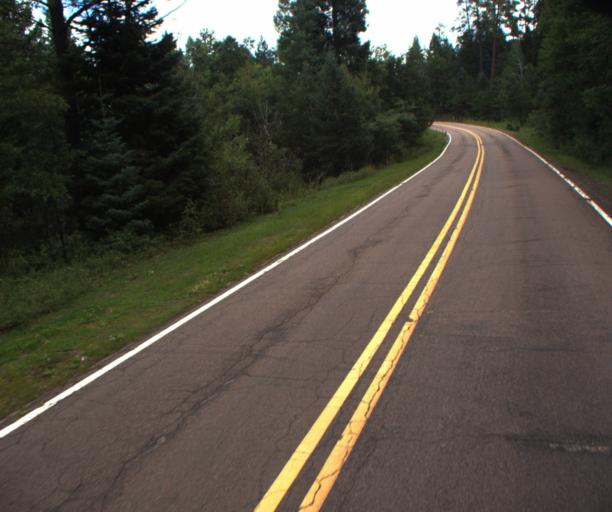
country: US
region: Arizona
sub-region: Navajo County
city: Pinetop-Lakeside
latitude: 34.0283
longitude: -109.7632
